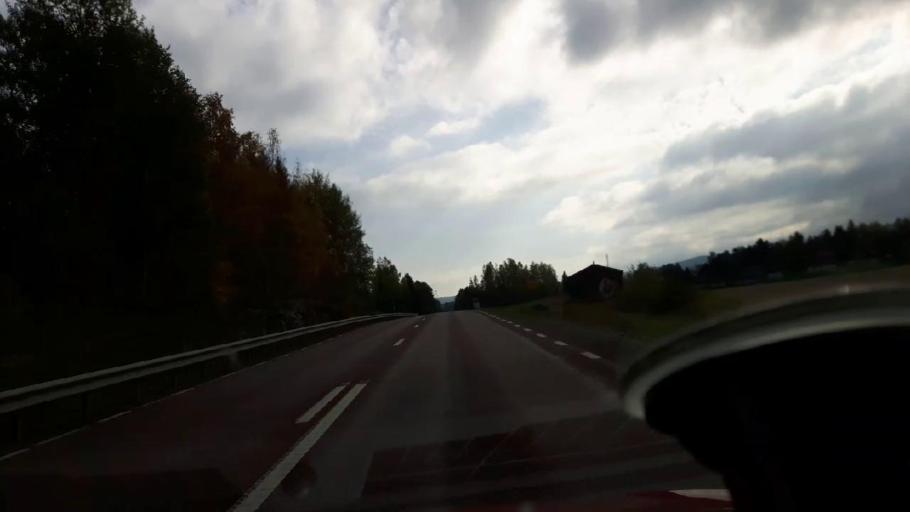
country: SE
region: Gaevleborg
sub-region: Bollnas Kommun
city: Kilafors
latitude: 61.2362
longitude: 16.5545
